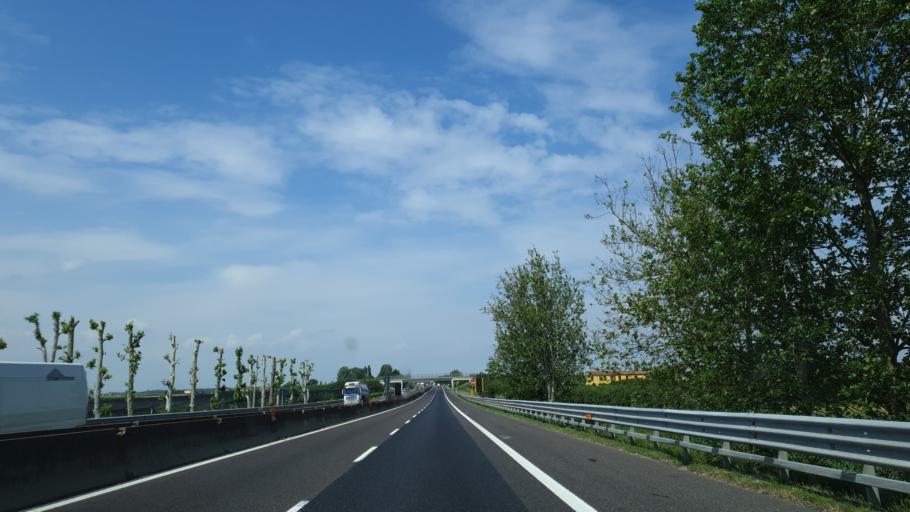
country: IT
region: Emilia-Romagna
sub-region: Provincia di Bologna
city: Malalbergo
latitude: 44.7388
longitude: 11.5205
